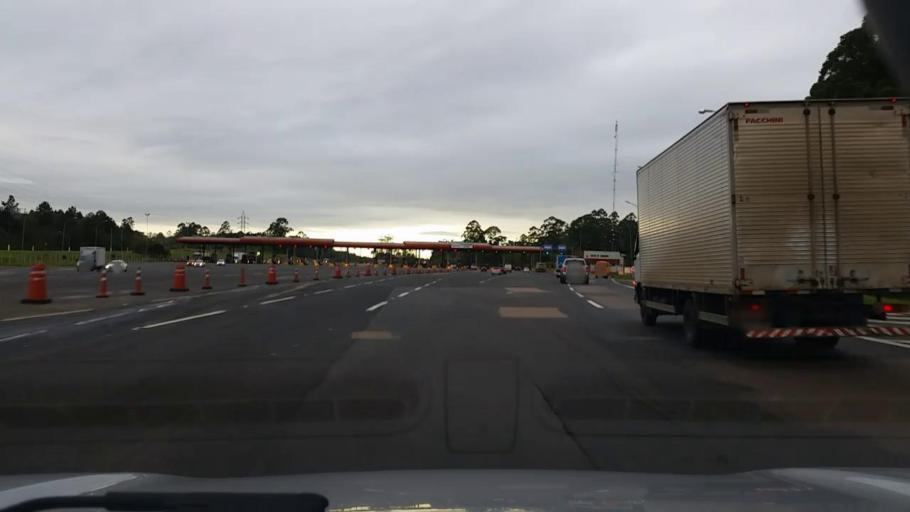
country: BR
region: Rio Grande do Sul
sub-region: Gravatai
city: Gravatai
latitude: -29.9548
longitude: -51.0341
